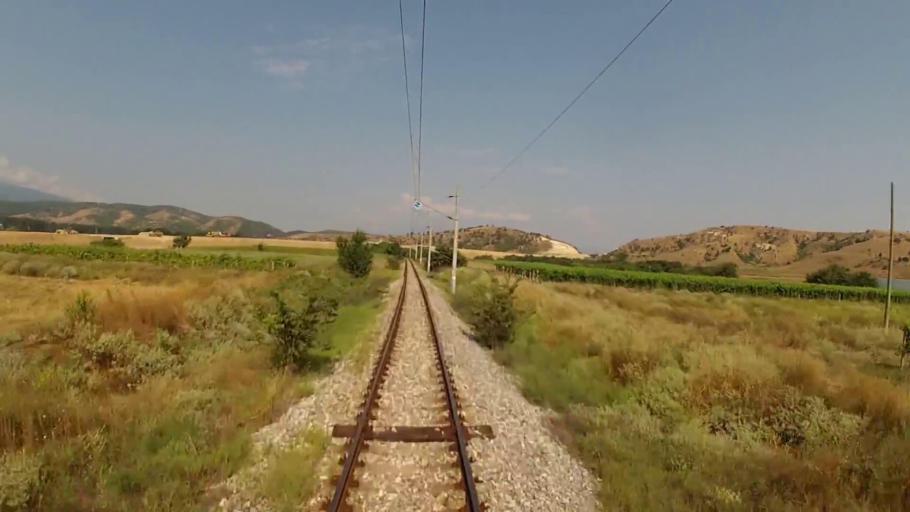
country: BG
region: Blagoevgrad
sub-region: Obshtina Petrich
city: Petrich
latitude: 41.4156
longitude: 23.3303
